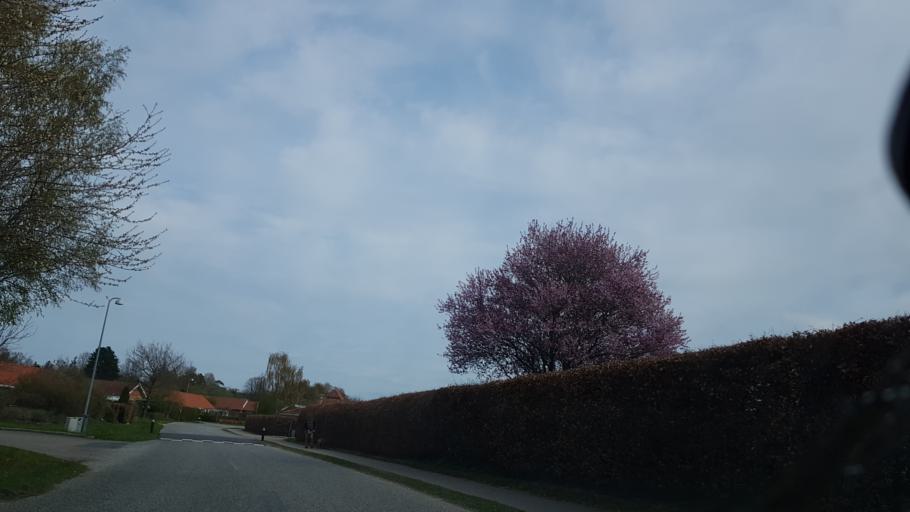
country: DK
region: Capital Region
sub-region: Allerod Kommune
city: Lillerod
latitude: 55.8844
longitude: 12.3391
